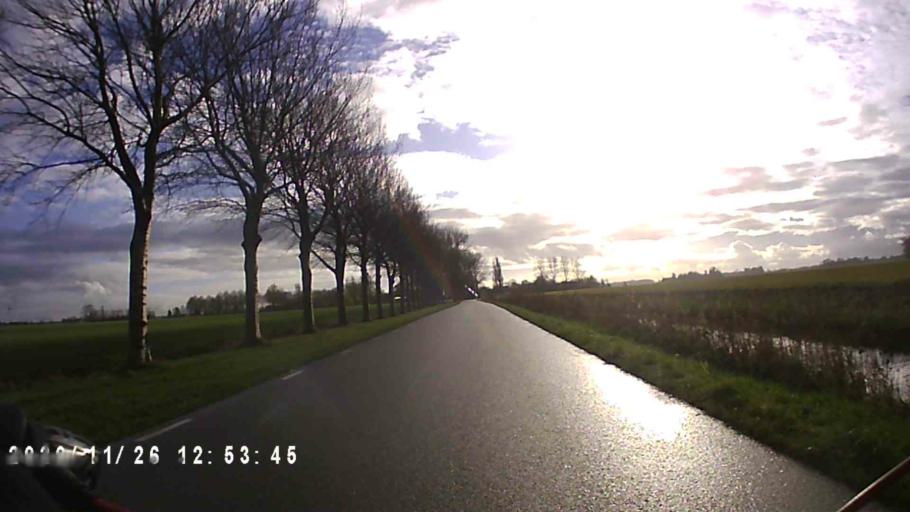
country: NL
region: Groningen
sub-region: Gemeente Appingedam
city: Appingedam
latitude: 53.3503
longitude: 6.7925
